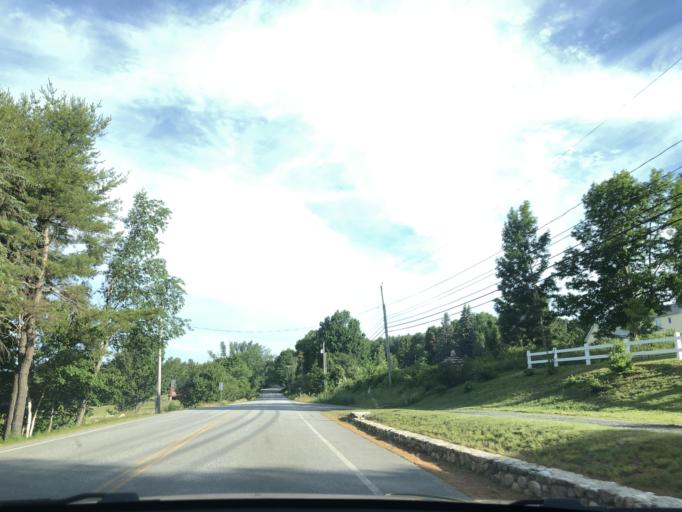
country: US
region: New Hampshire
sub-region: Merrimack County
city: New London
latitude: 43.4010
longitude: -71.9652
